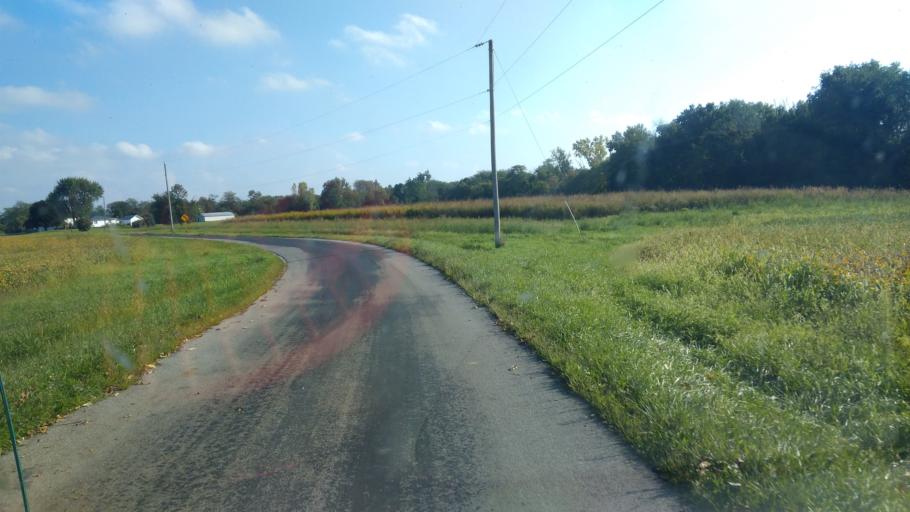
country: US
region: Ohio
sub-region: Hardin County
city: Forest
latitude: 40.7214
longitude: -83.4602
